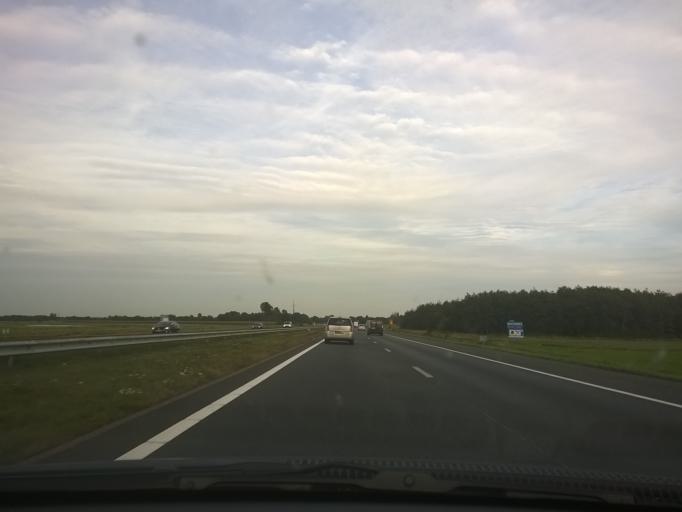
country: NL
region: Groningen
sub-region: Gemeente Grootegast
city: Grootegast
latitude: 53.1482
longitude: 6.2512
